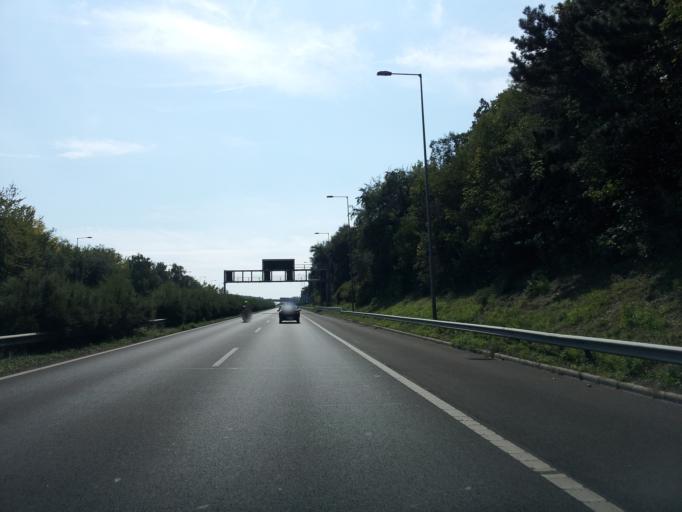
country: HU
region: Pest
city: Toeroekbalint
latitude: 47.4404
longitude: 18.9036
